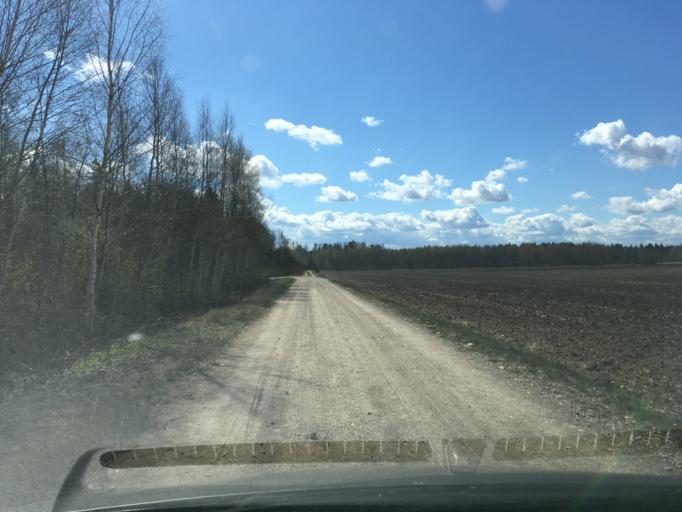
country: EE
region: Harju
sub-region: Raasiku vald
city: Raasiku
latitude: 59.2115
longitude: 25.1440
